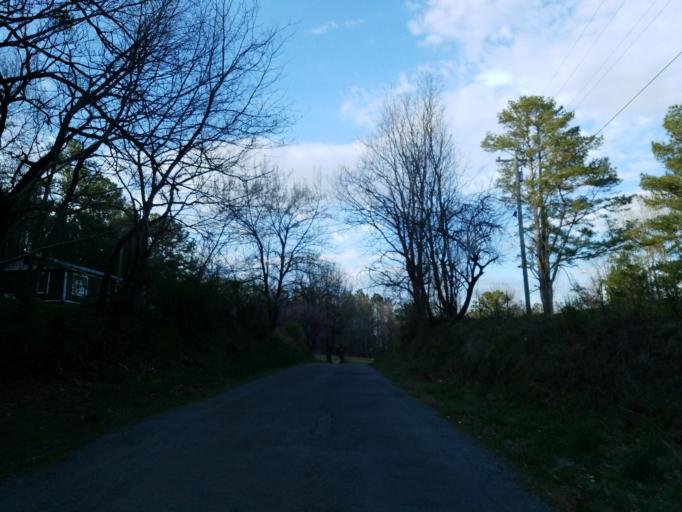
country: US
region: Georgia
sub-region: Bartow County
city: Rydal
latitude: 34.5102
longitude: -84.6298
